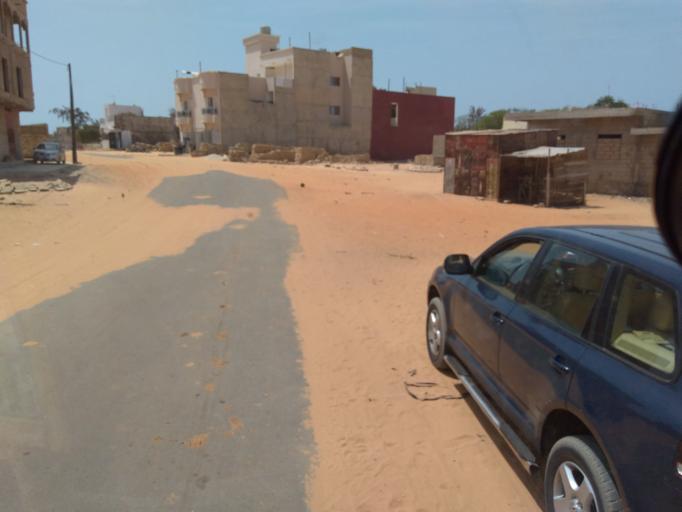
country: SN
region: Dakar
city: Pikine
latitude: 14.7856
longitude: -17.3345
